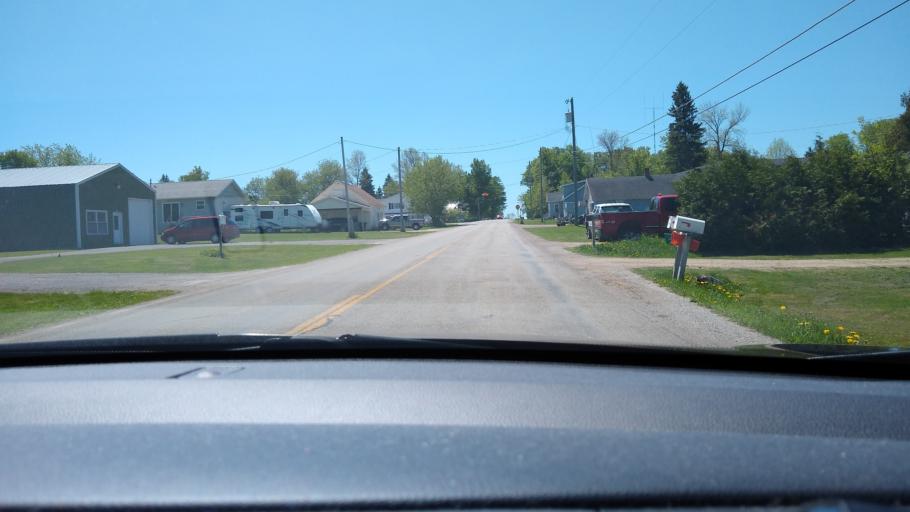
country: US
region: Michigan
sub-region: Delta County
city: Escanaba
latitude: 45.8273
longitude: -87.1831
